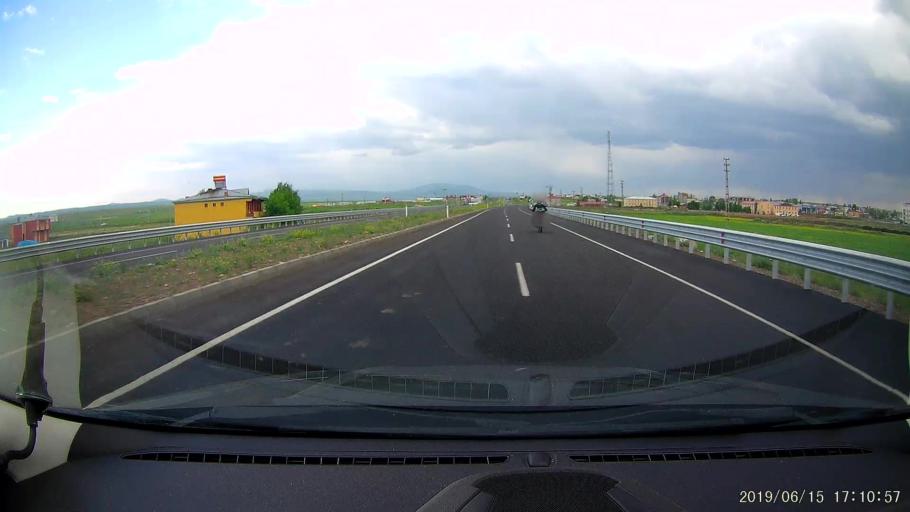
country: TR
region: Kars
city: Kars
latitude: 40.6164
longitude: 43.1333
